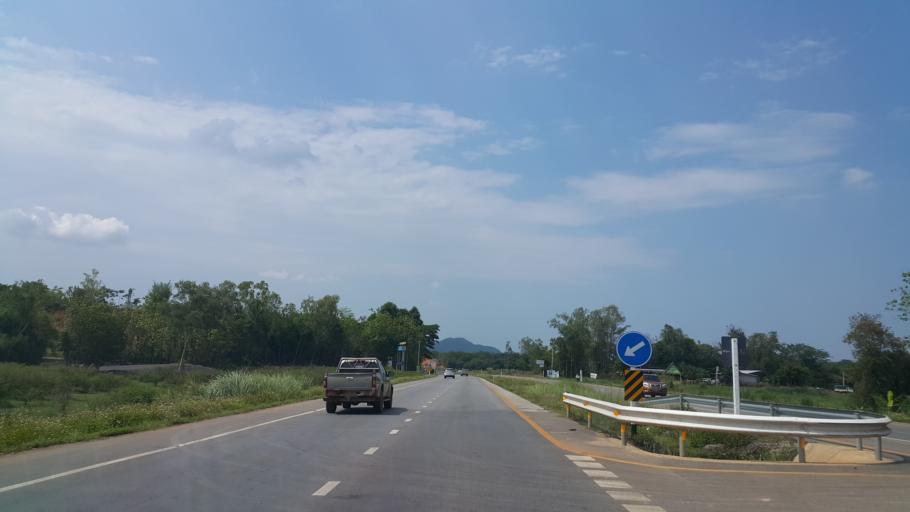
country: TH
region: Chiang Rai
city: Chiang Rai
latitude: 19.9845
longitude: 99.8907
